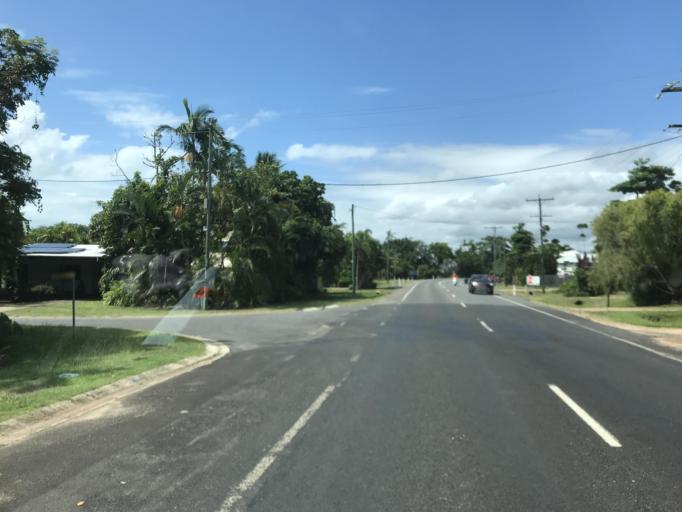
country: AU
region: Queensland
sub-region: Cassowary Coast
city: Innisfail
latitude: -17.8689
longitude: 146.1065
